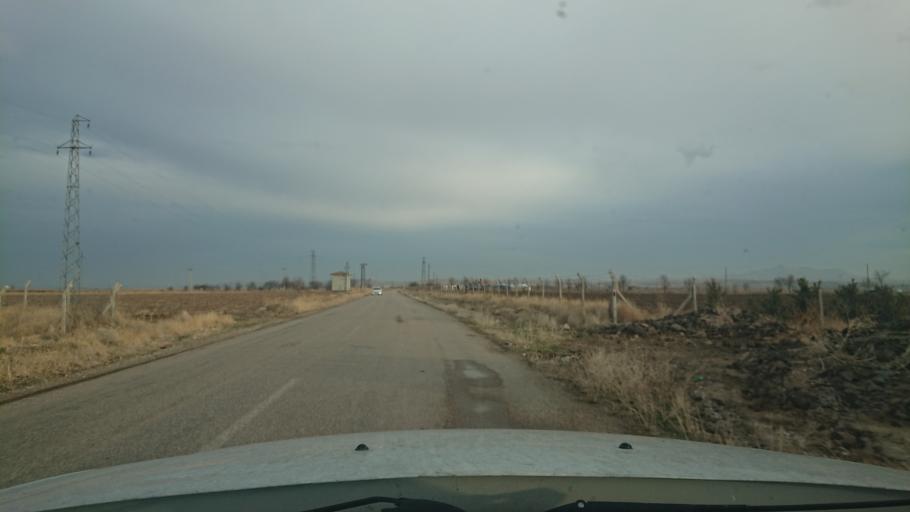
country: TR
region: Aksaray
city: Yesilova
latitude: 38.4260
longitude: 33.8350
